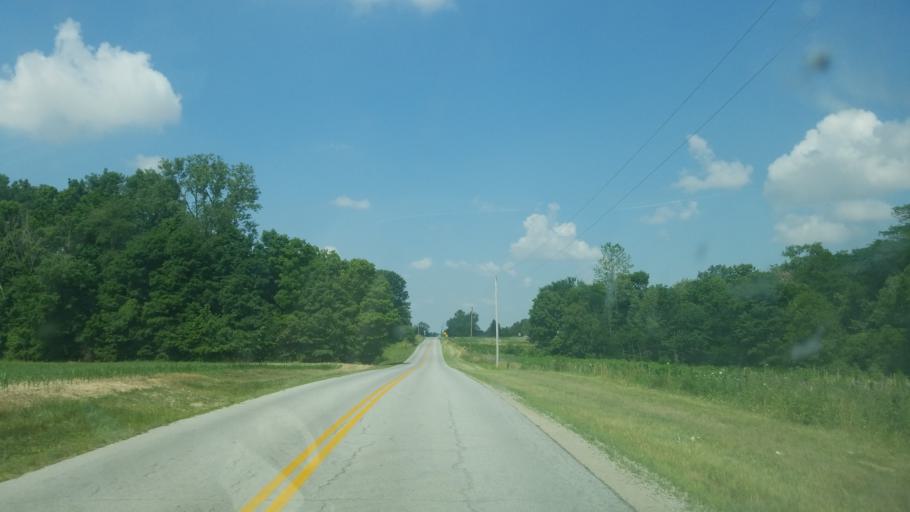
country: US
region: Ohio
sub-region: Auglaize County
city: Cridersville
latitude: 40.5711
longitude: -84.0739
